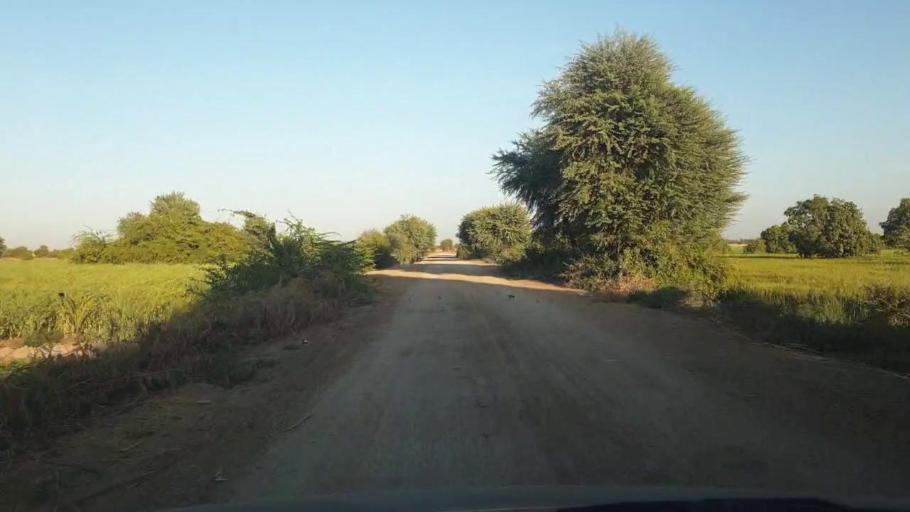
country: PK
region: Sindh
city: Dhoro Naro
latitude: 25.3749
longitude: 69.5756
